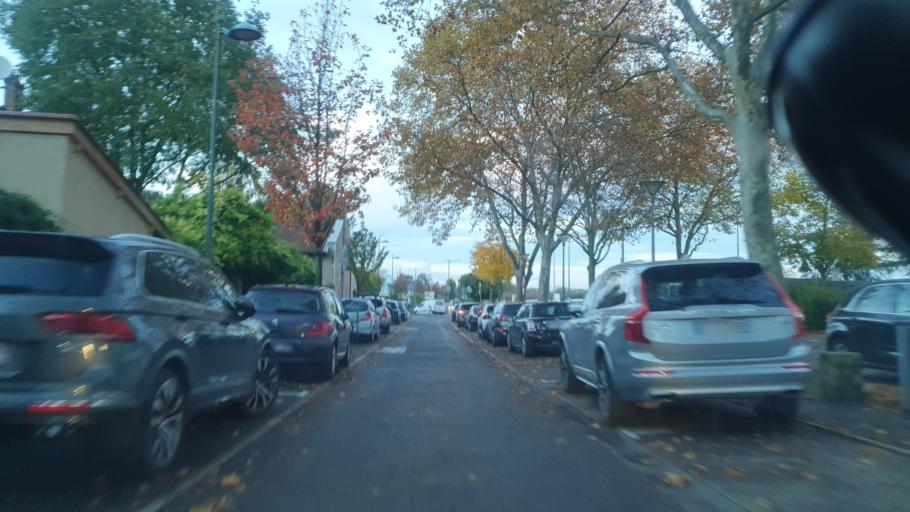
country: FR
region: Rhone-Alpes
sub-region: Departement du Rhone
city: Rochetaillee-sur-Saone
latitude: 45.8461
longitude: 4.8317
